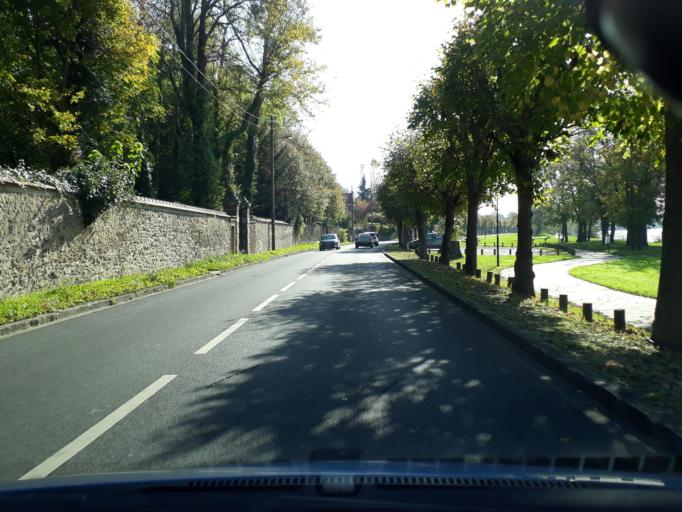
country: FR
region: Ile-de-France
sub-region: Departement de Seine-et-Marne
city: Melun
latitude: 48.5296
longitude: 2.6701
